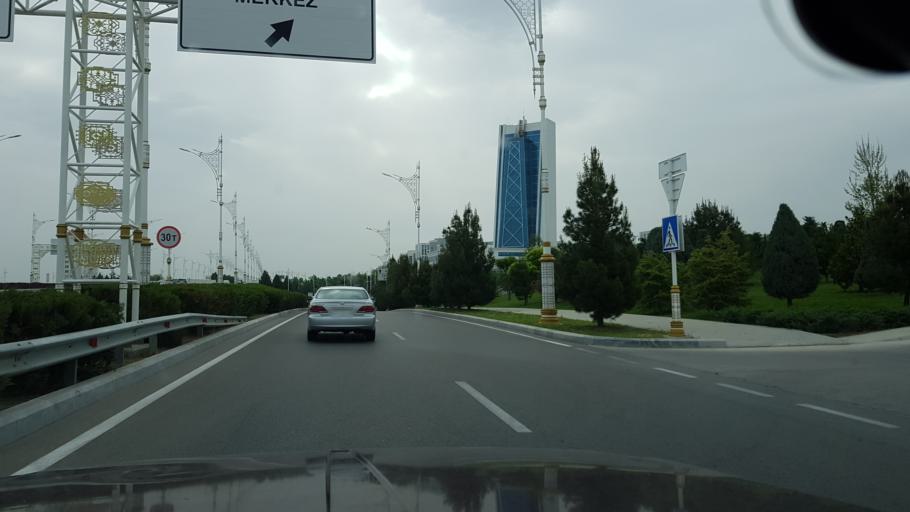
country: TM
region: Ahal
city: Ashgabat
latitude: 37.8789
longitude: 58.3839
